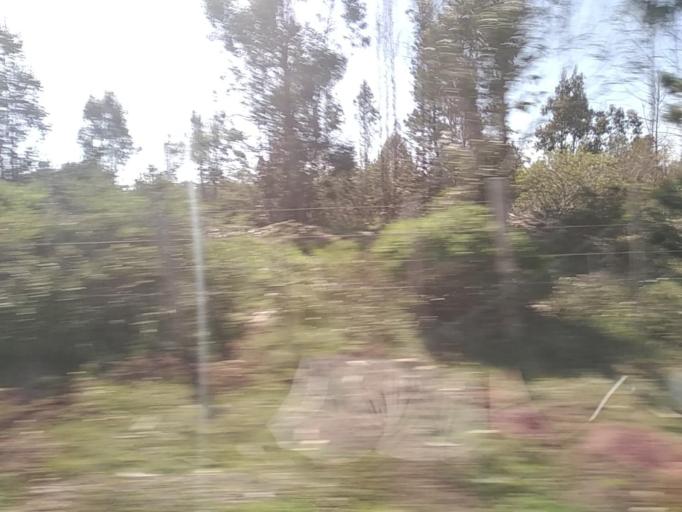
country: CL
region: Valparaiso
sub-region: San Antonio Province
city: El Tabo
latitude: -33.4095
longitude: -71.5929
